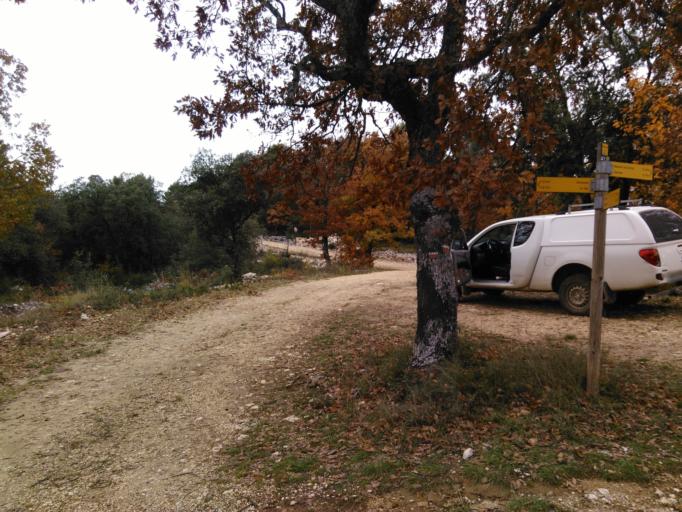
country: FR
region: Provence-Alpes-Cote d'Azur
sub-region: Departement du Vaucluse
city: Venasque
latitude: 43.9901
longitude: 5.1870
